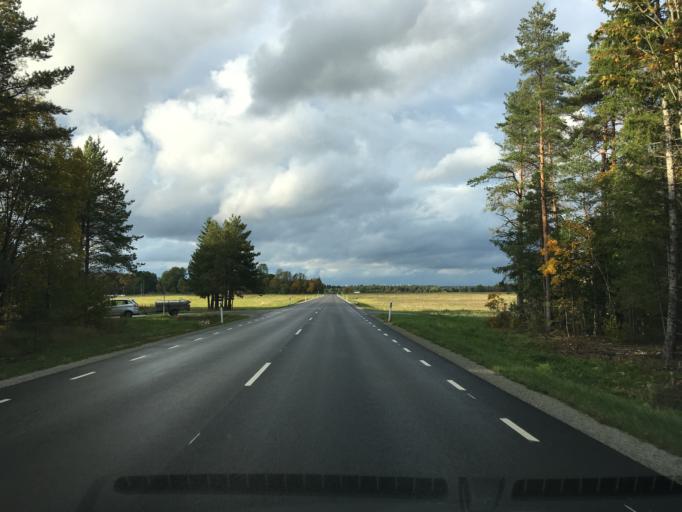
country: EE
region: Harju
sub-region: Paldiski linn
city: Paldiski
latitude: 59.2057
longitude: 24.0958
